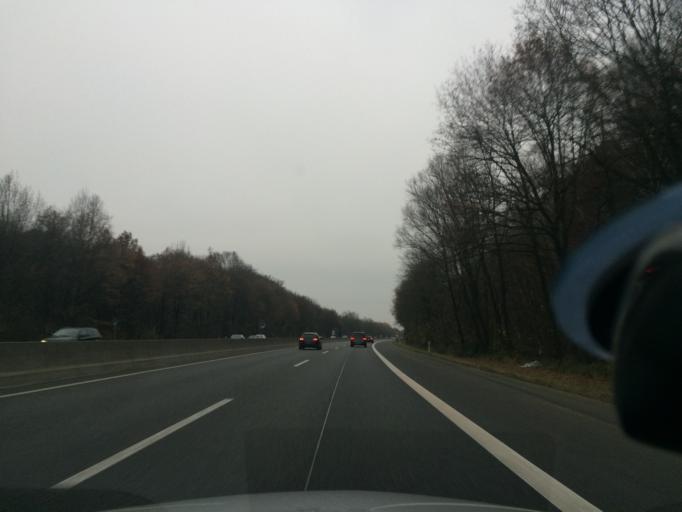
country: DE
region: Hesse
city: Dreieich
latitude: 50.0010
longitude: 8.6911
